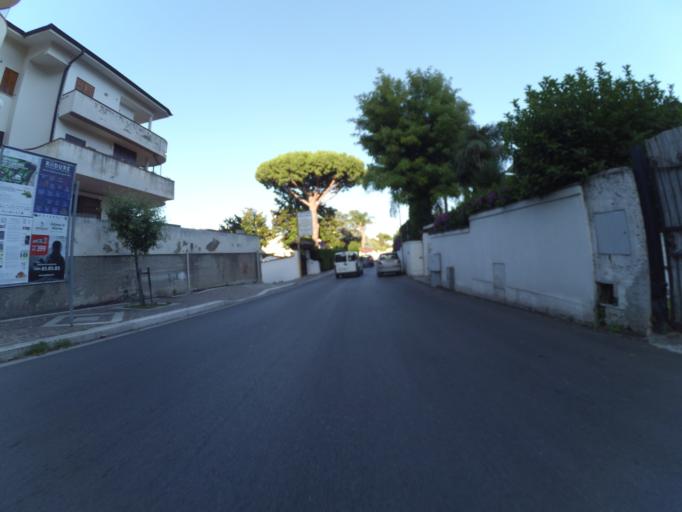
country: IT
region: Latium
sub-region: Provincia di Latina
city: San Felice Circeo
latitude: 41.2412
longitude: 13.0922
